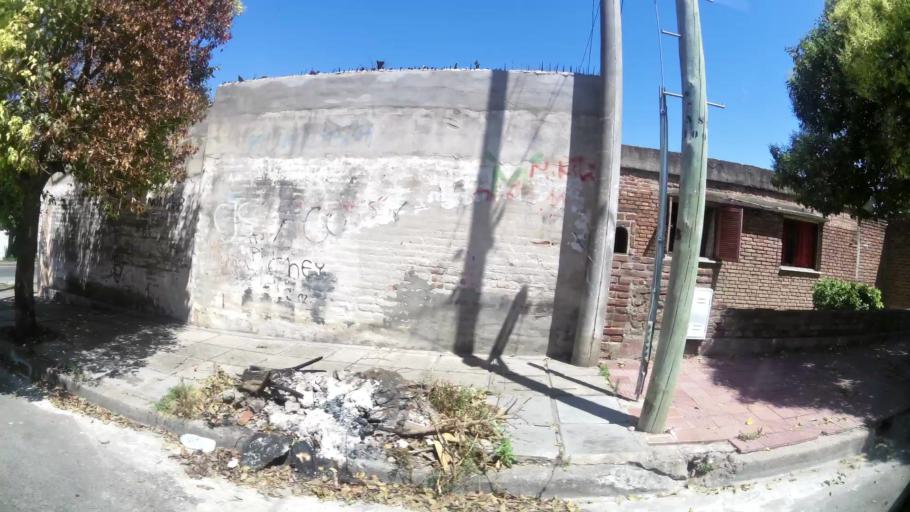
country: AR
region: Cordoba
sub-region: Departamento de Capital
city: Cordoba
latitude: -31.4344
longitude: -64.2094
